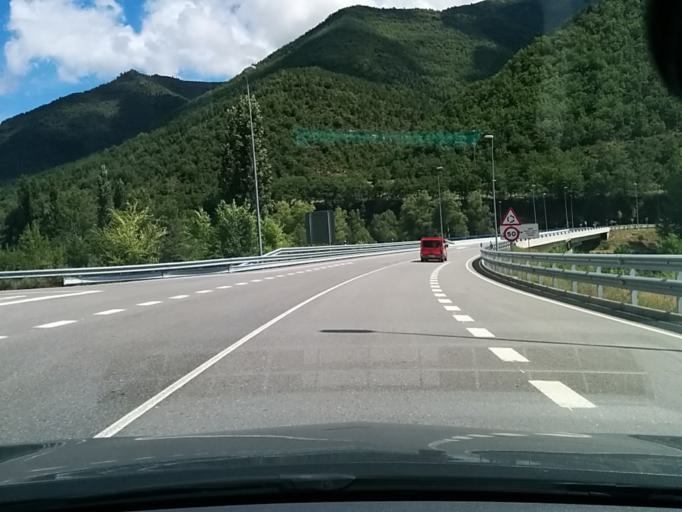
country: ES
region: Aragon
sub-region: Provincia de Huesca
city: Fiscal
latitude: 42.5002
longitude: -0.1204
